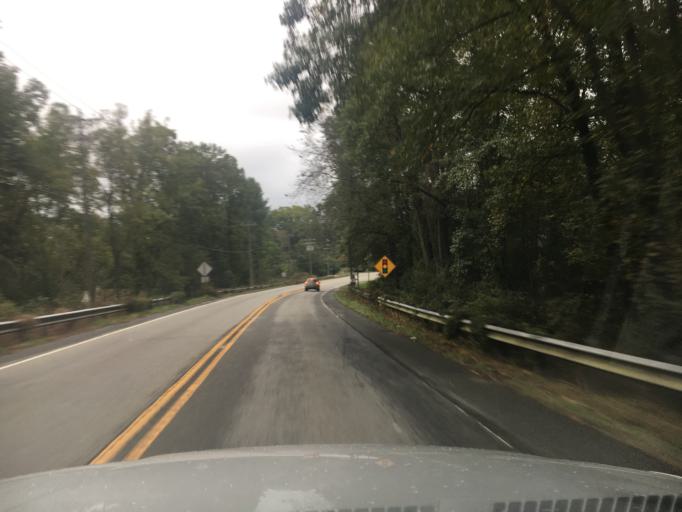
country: US
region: North Carolina
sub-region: Henderson County
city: Horse Shoe
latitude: 35.3420
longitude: -82.5590
